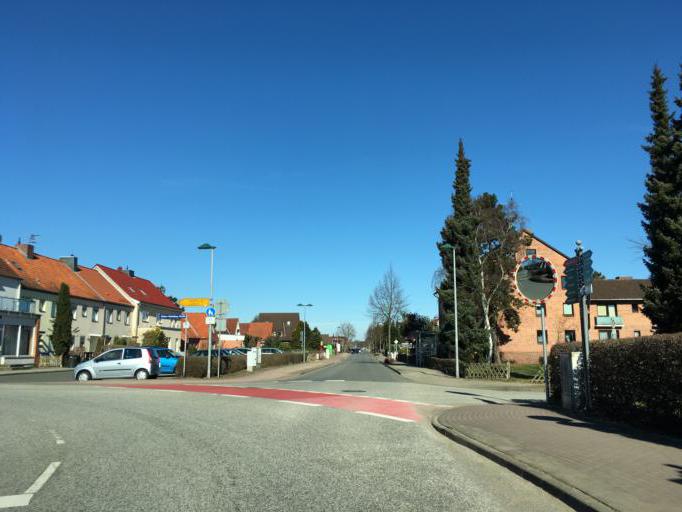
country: DE
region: Schleswig-Holstein
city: Molln
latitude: 53.6156
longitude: 10.6968
